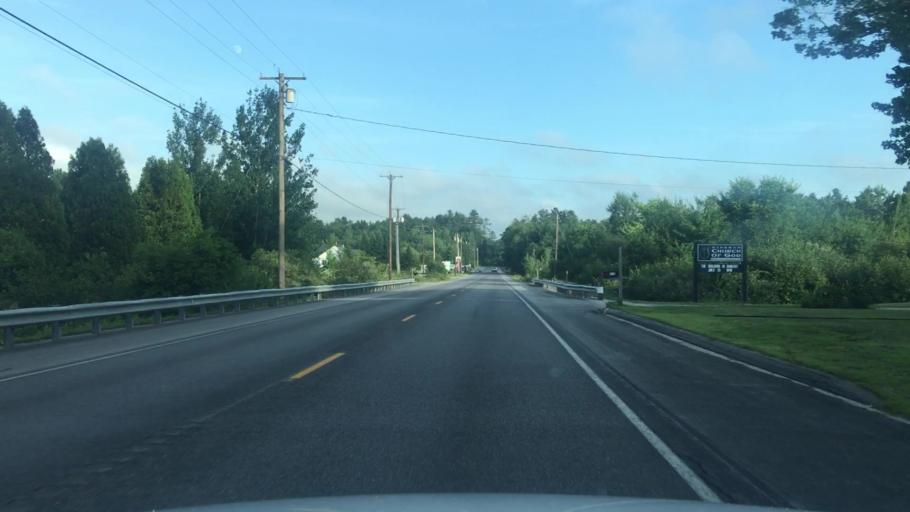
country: US
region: Maine
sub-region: Cumberland County
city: North Windham
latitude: 43.7981
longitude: -70.4020
